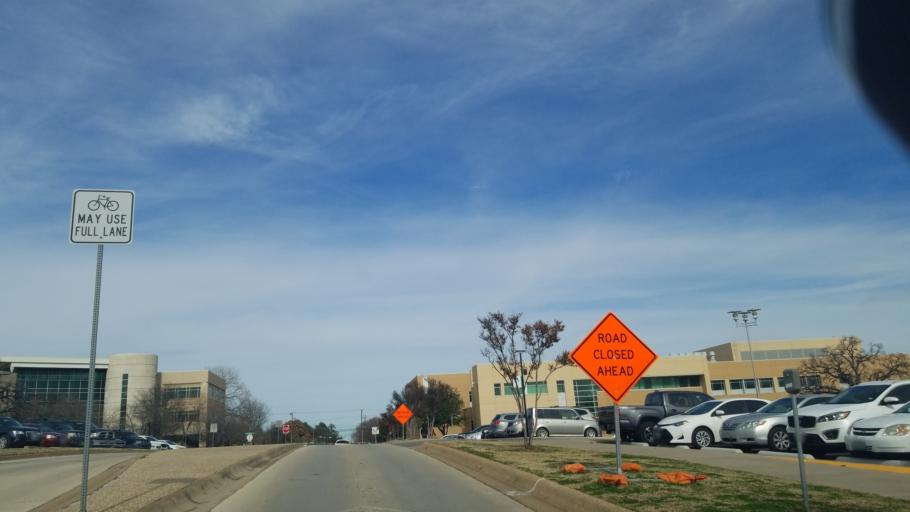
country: US
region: Texas
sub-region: Denton County
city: Denton
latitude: 33.2128
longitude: -97.1506
